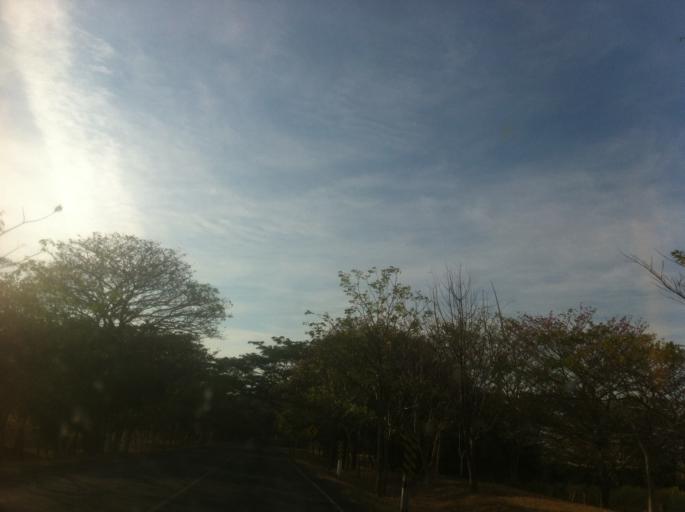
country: NI
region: Rivas
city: San Jorge
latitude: 11.3175
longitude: -85.7110
